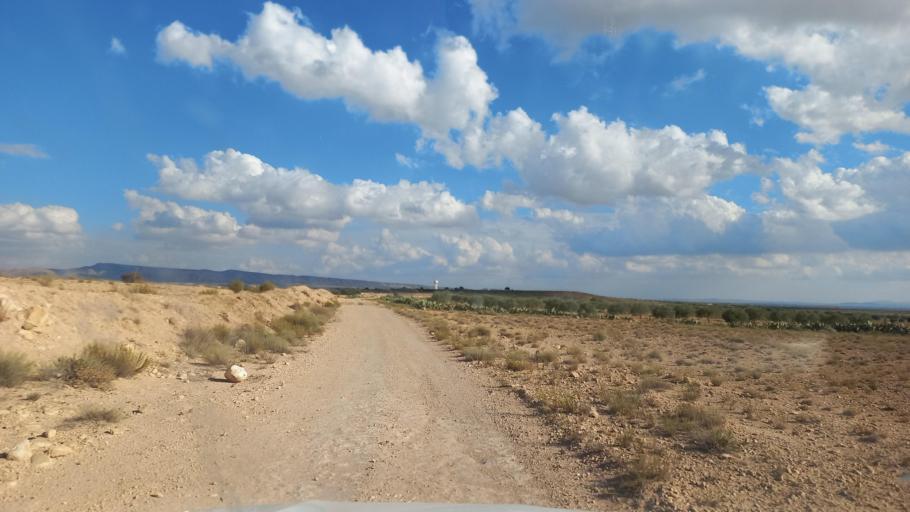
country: TN
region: Al Qasrayn
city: Sbiba
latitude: 35.3980
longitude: 9.0368
